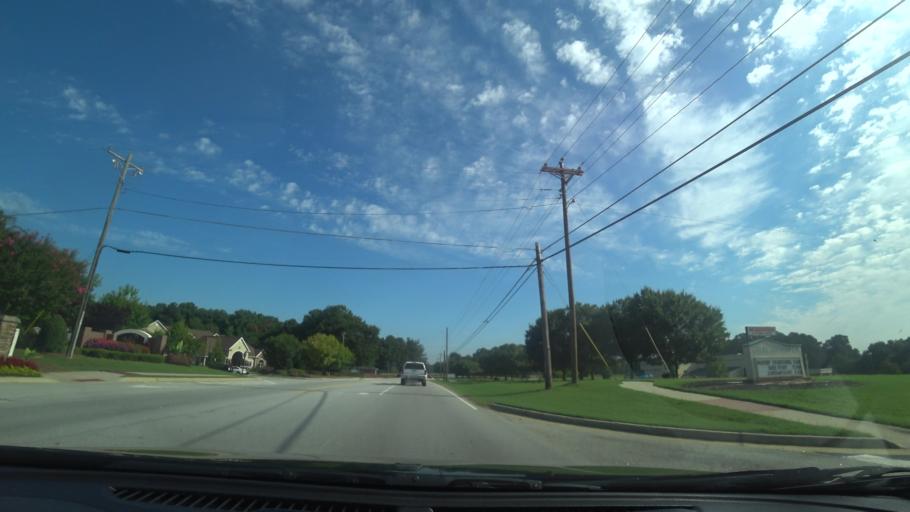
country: US
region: Georgia
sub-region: Gwinnett County
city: Grayson
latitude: 33.8646
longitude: -83.9571
